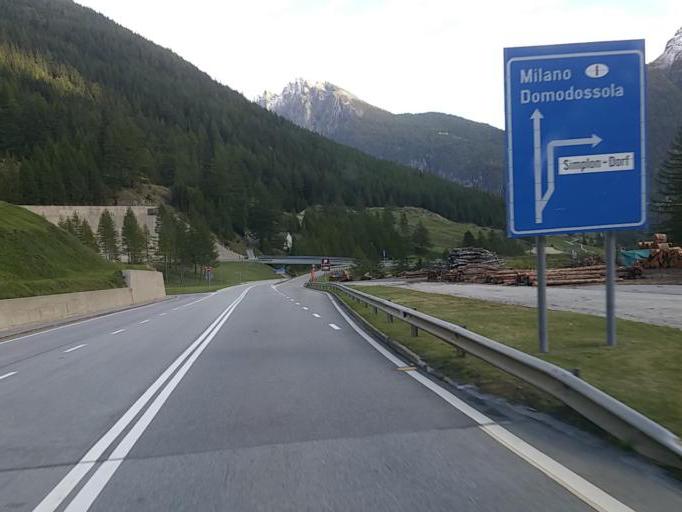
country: CH
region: Valais
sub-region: Brig District
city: Brig
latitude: 46.2007
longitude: 8.0544
